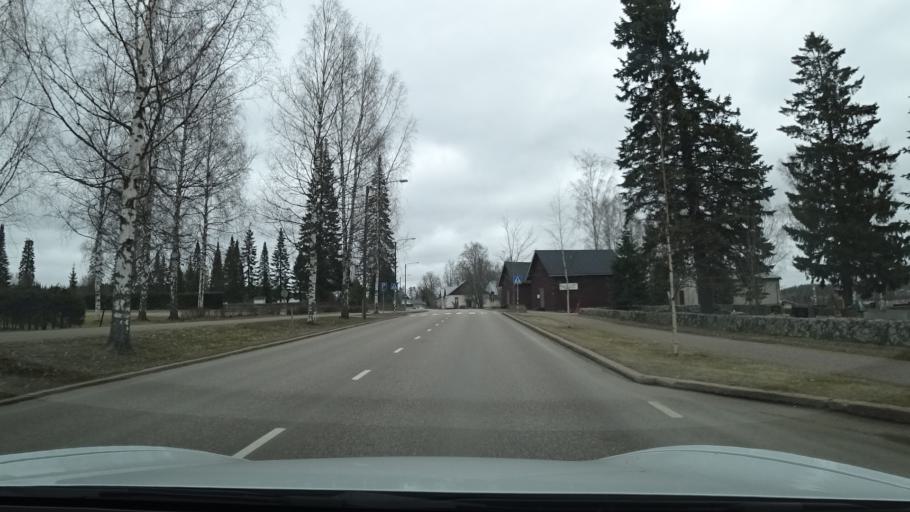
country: FI
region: Uusimaa
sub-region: Porvoo
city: Myrskylae
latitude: 60.6670
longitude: 25.8509
